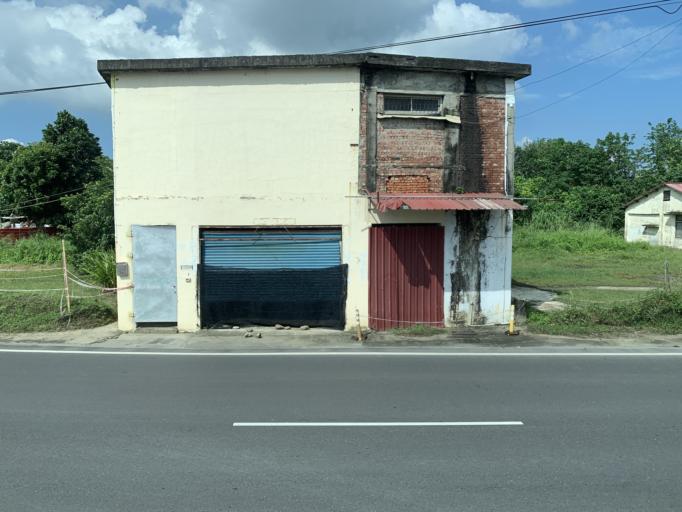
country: TW
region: Taiwan
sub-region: Pingtung
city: Pingtung
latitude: 22.8726
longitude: 120.4976
